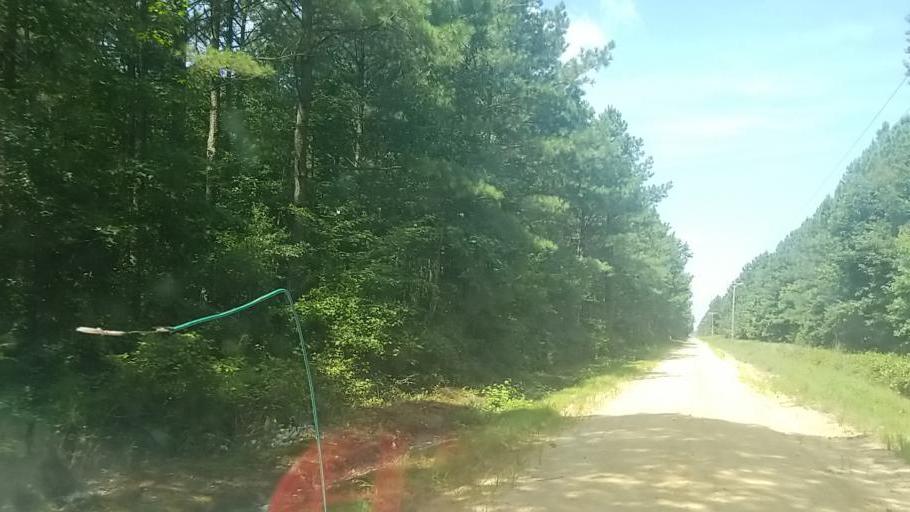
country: US
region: Maryland
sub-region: Caroline County
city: Denton
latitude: 38.8678
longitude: -75.7343
